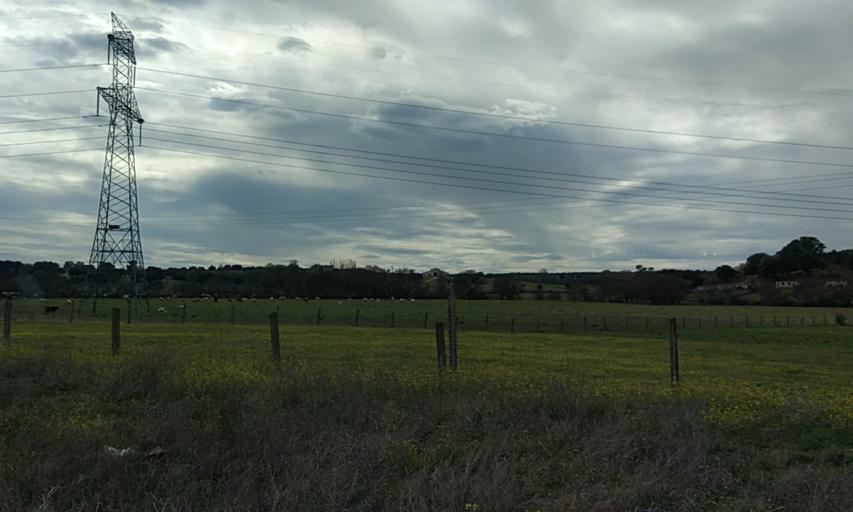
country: ES
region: Castille and Leon
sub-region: Provincia de Salamanca
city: Ciudad Rodrigo
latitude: 40.5511
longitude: -6.5586
